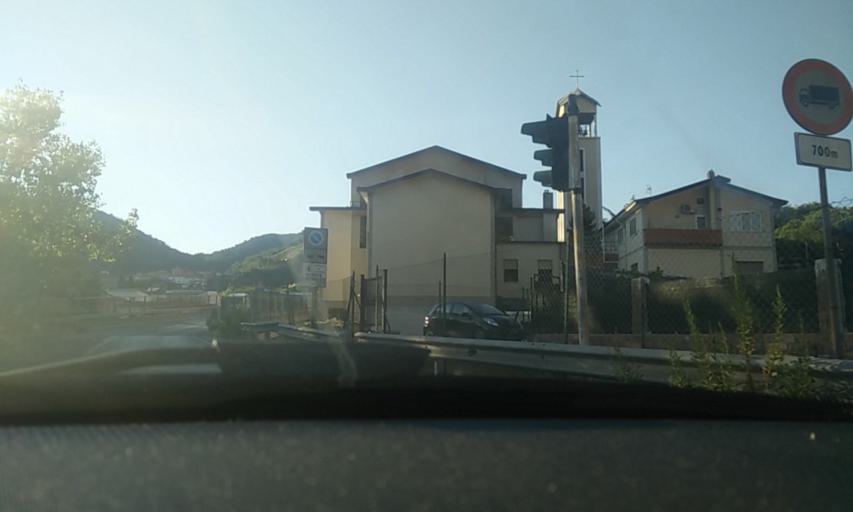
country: IT
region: Tuscany
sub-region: Provincia di Massa-Carrara
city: Carrara
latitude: 44.0684
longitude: 10.0865
